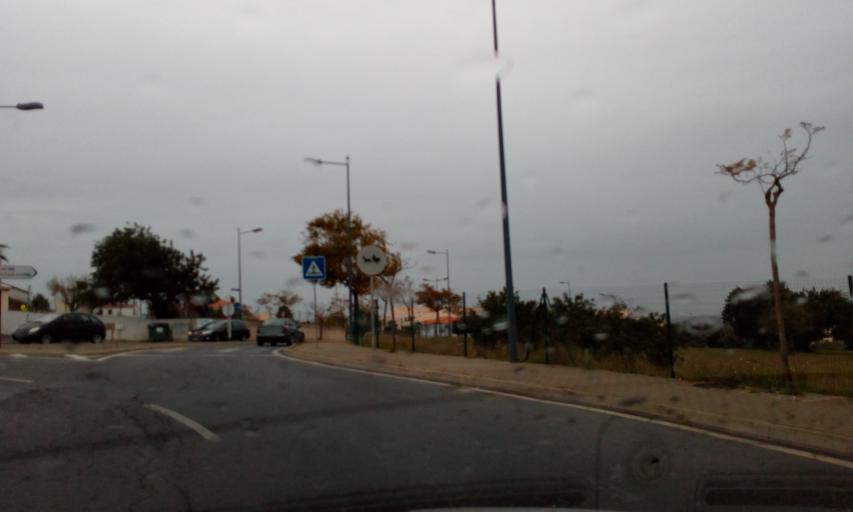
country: PT
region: Faro
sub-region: Albufeira
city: Ferreiras
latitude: 37.1159
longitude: -8.2293
